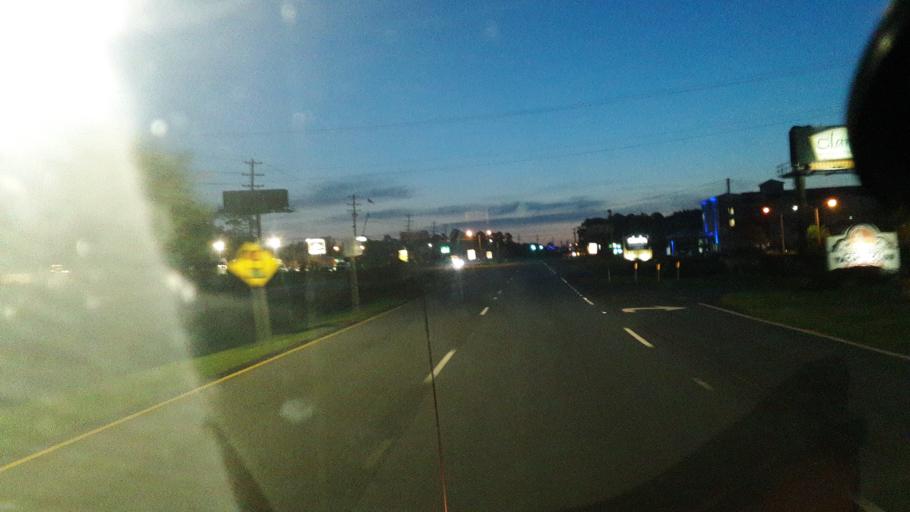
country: US
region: South Carolina
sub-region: Horry County
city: Little River
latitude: 33.8661
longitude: -78.6400
